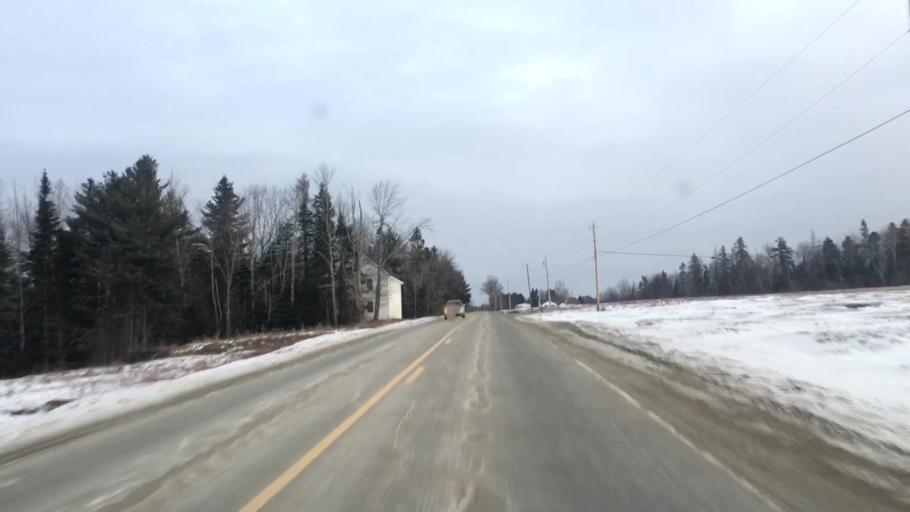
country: US
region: Maine
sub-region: Hancock County
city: Franklin
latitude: 44.7110
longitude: -68.3386
